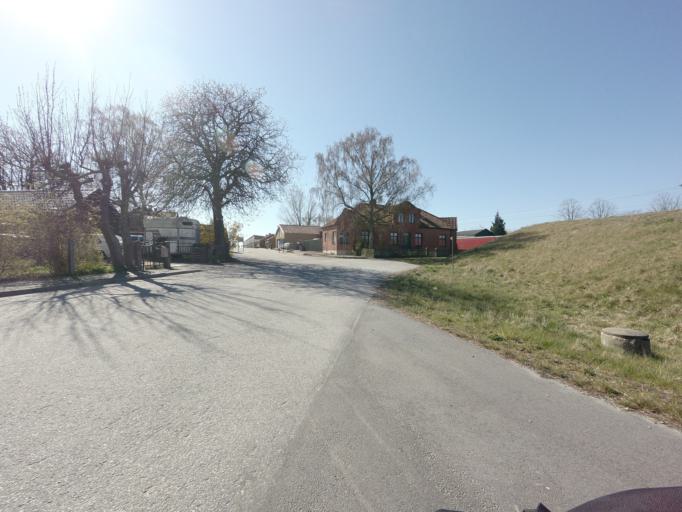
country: SE
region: Skane
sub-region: Malmo
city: Oxie
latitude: 55.4645
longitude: 13.1351
